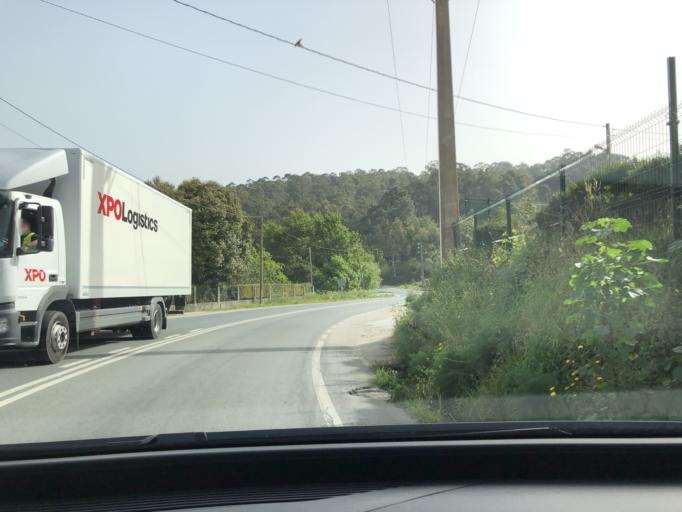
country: ES
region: Galicia
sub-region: Provincia de Pontevedra
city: Marin
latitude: 42.3747
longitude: -8.7268
